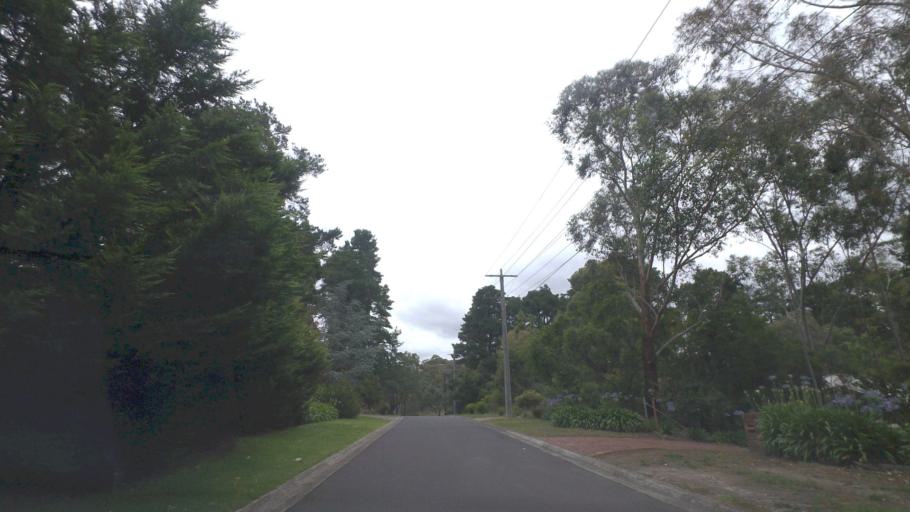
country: AU
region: Victoria
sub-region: Manningham
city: Park Orchards
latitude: -37.7878
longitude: 145.2124
